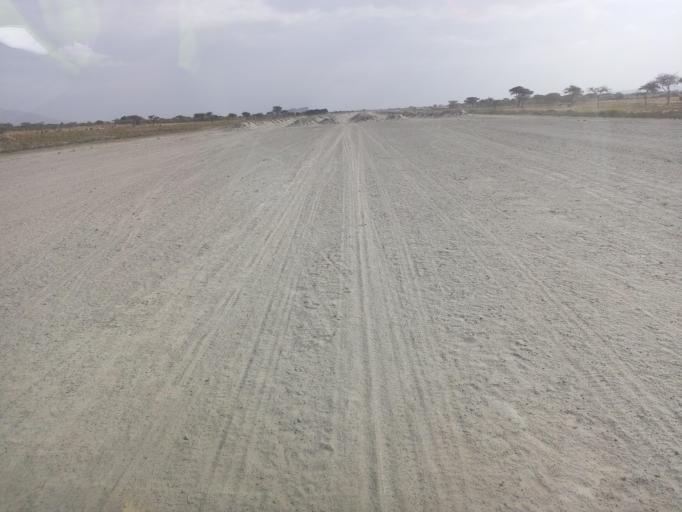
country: ET
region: Oromiya
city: Ziway
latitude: 7.8797
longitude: 38.6732
